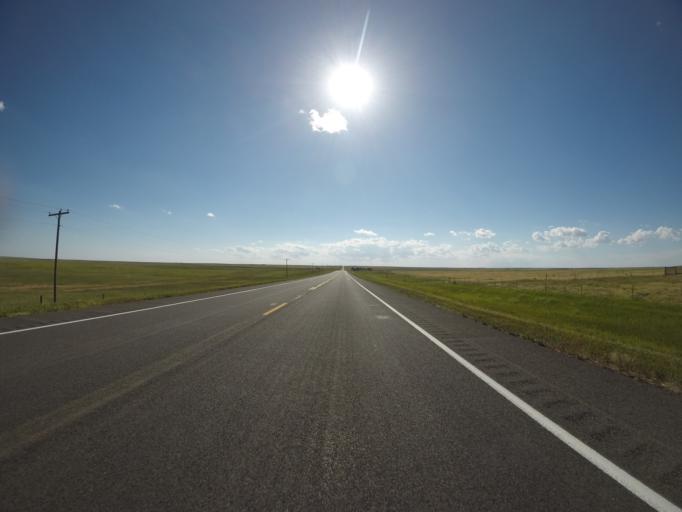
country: US
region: Colorado
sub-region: Morgan County
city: Brush
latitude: 40.6106
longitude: -103.6146
